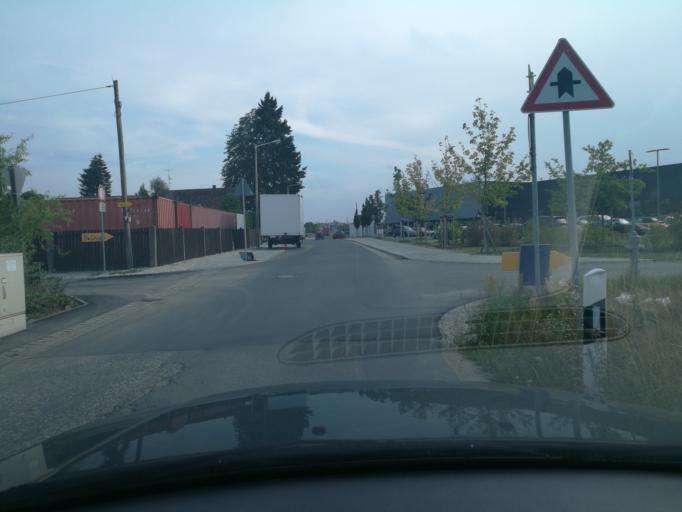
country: DE
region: Bavaria
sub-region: Regierungsbezirk Mittelfranken
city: Wetzendorf
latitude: 49.4857
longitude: 11.0605
